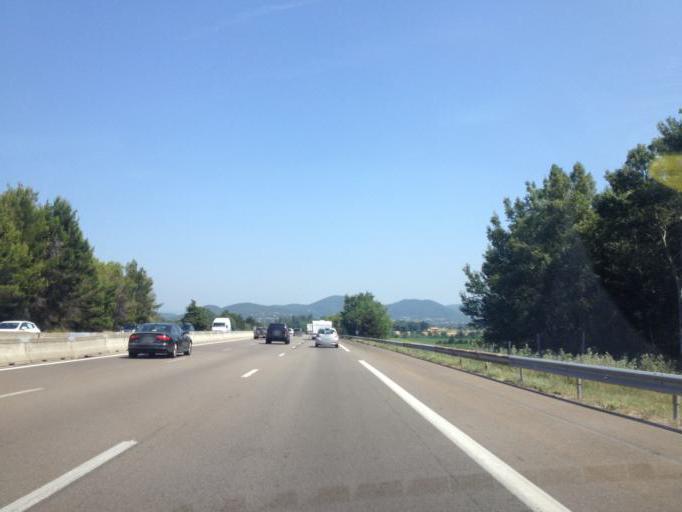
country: FR
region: Rhone-Alpes
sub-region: Departement de la Drome
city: Montboucher-sur-Jabron
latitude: 44.5572
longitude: 4.8115
